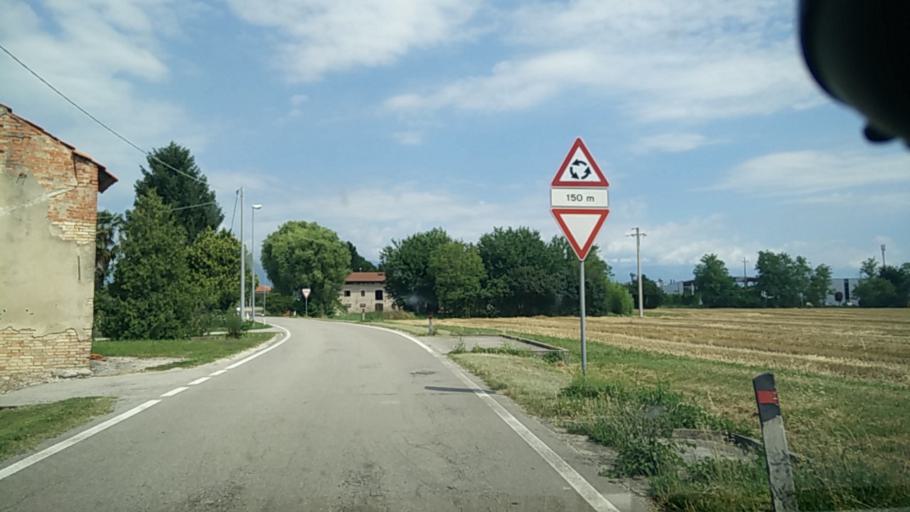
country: IT
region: Veneto
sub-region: Provincia di Treviso
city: Portobuffole
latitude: 45.8581
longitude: 12.5449
